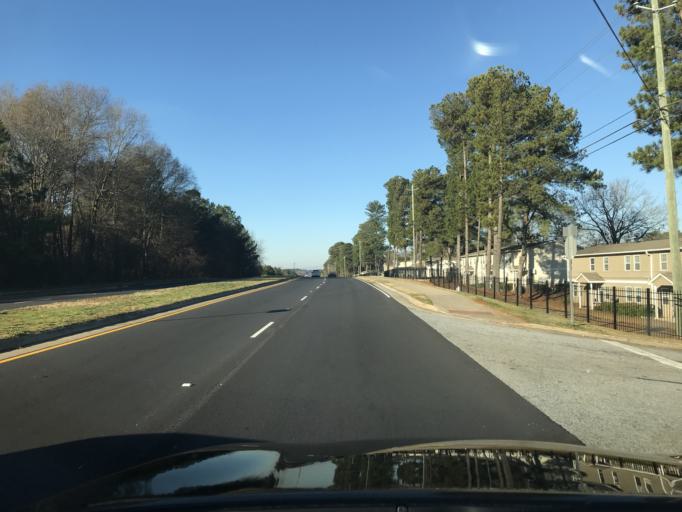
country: US
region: Georgia
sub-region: Clayton County
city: Jonesboro
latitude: 33.5179
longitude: -84.3662
